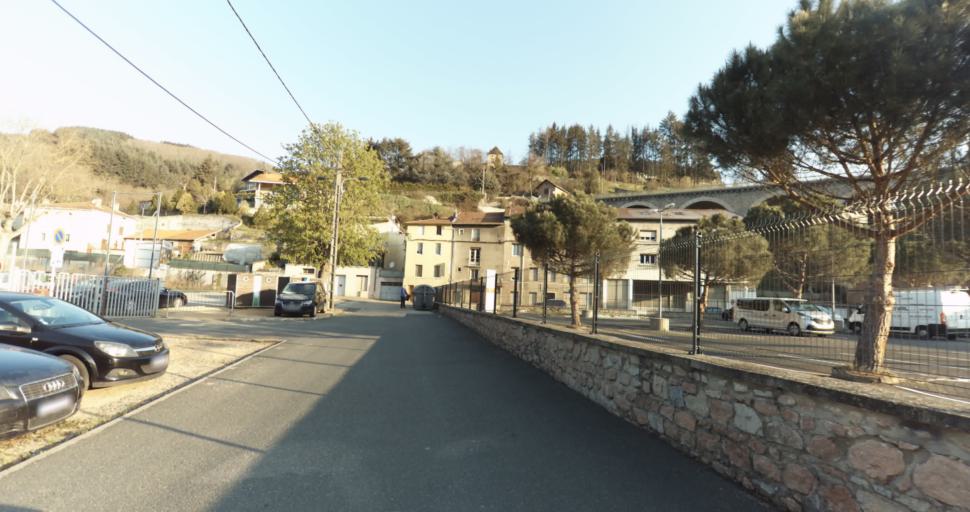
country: FR
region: Rhone-Alpes
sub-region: Departement du Rhone
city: Tarare
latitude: 45.8947
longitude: 4.4234
